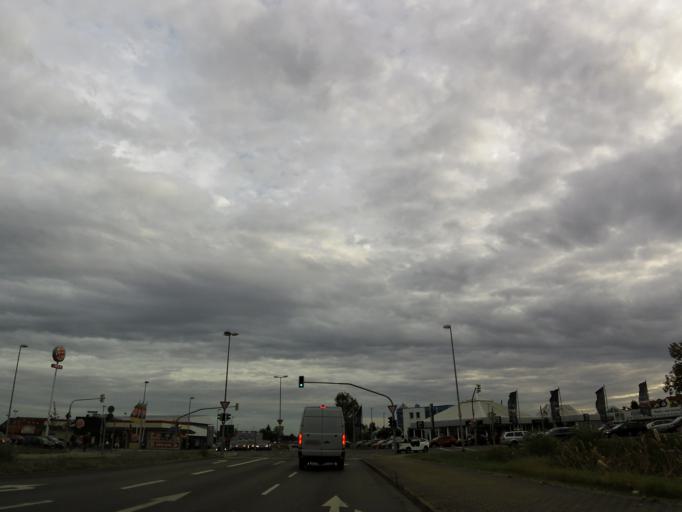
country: DE
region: Saxony
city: Markranstadt
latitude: 51.3468
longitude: 12.2625
